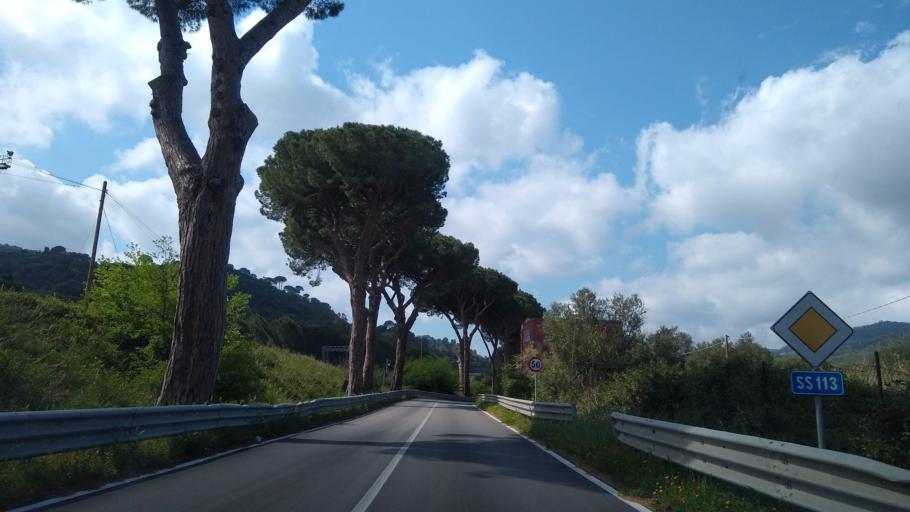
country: IT
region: Sicily
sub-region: Trapani
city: Calatafimi
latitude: 37.9381
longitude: 12.8548
